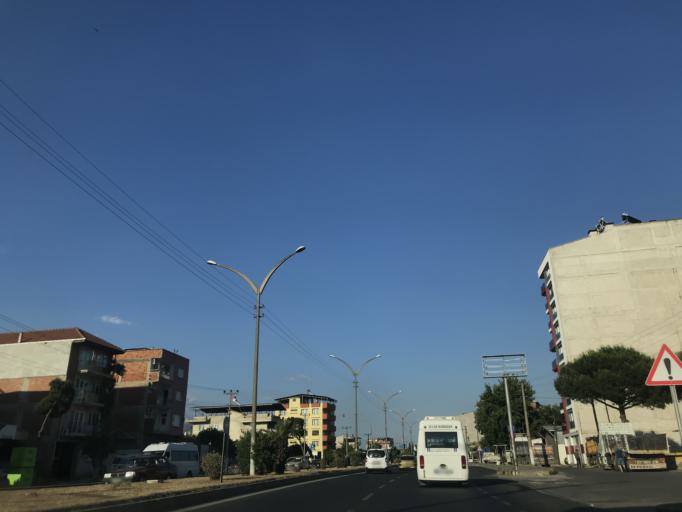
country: TR
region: Aydin
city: Umurlu
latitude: 37.8513
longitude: 27.9653
